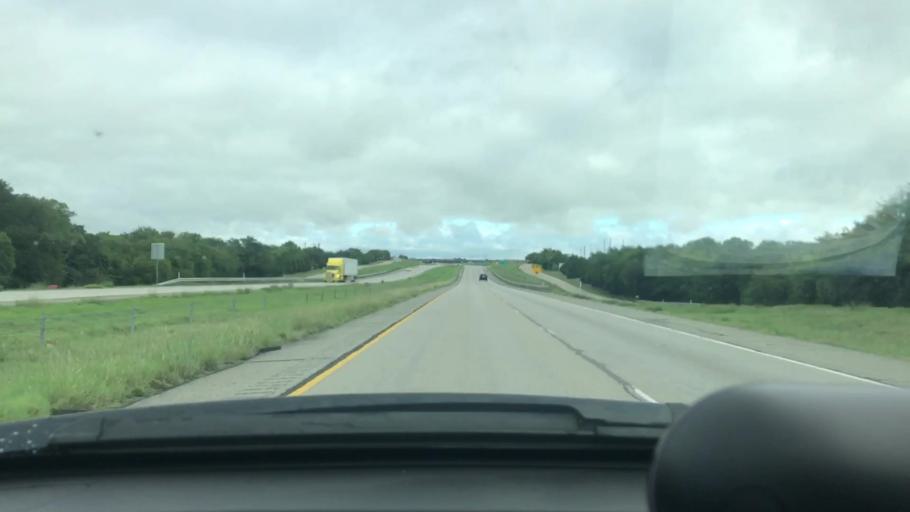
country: US
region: Texas
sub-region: Grayson County
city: Van Alstyne
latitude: 33.3919
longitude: -96.5804
